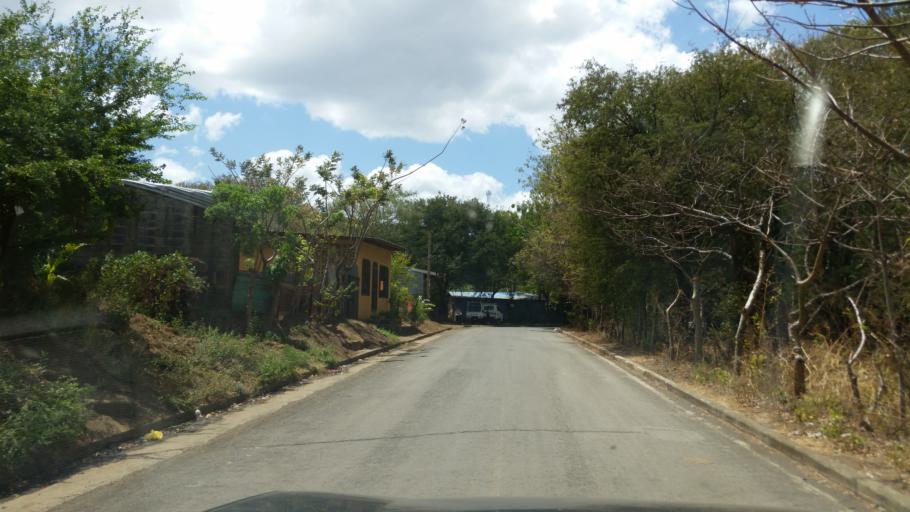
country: NI
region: Managua
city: Managua
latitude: 12.1073
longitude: -86.2170
